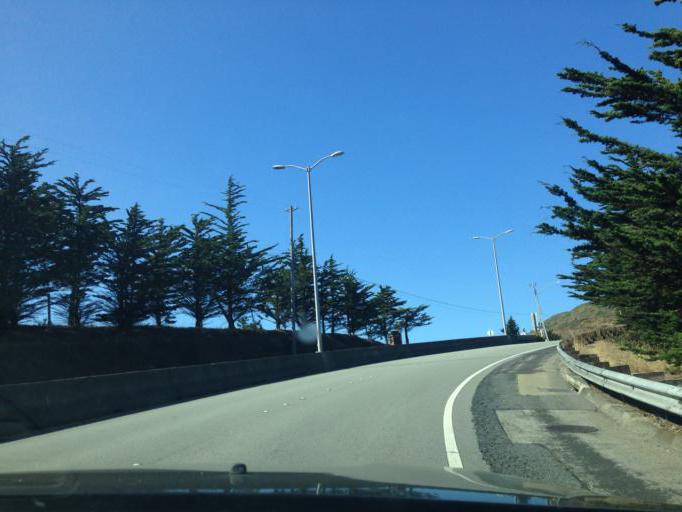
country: US
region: California
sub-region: San Mateo County
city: Pacifica
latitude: 37.6289
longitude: -122.4781
